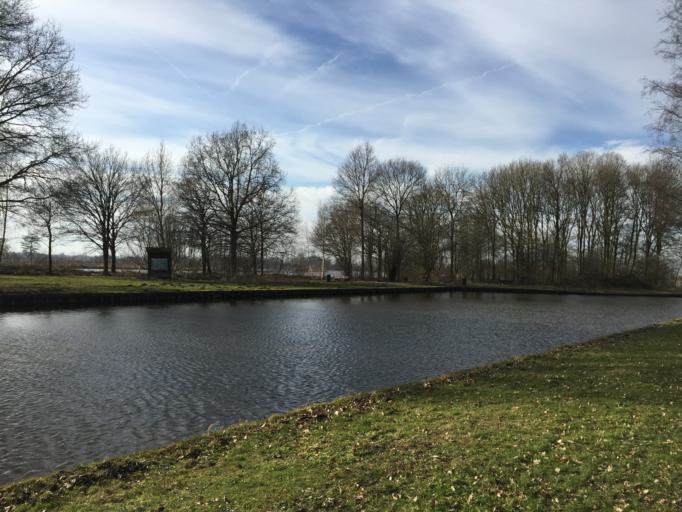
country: NL
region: South Holland
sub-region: Gemeente Vlist
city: Haastrecht
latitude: 52.0237
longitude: 4.7701
